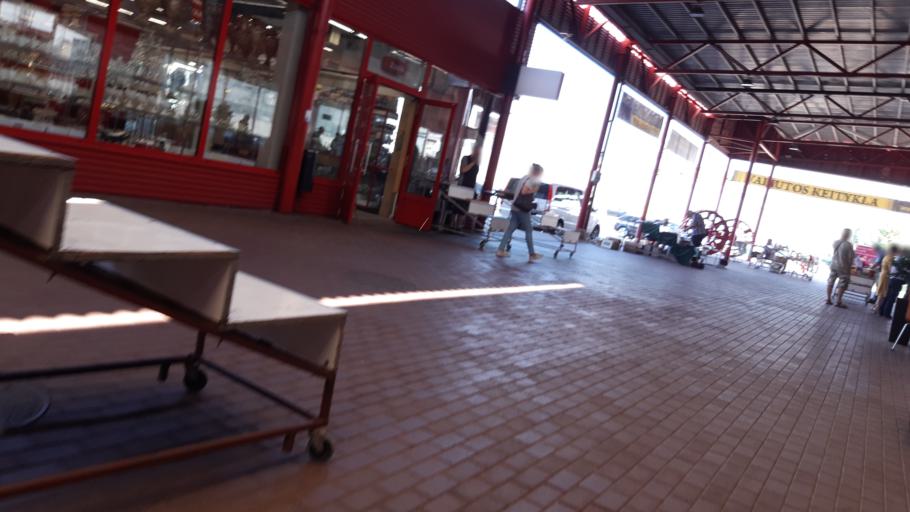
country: LT
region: Kauno apskritis
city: Dainava (Kaunas)
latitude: 54.9160
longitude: 23.9922
